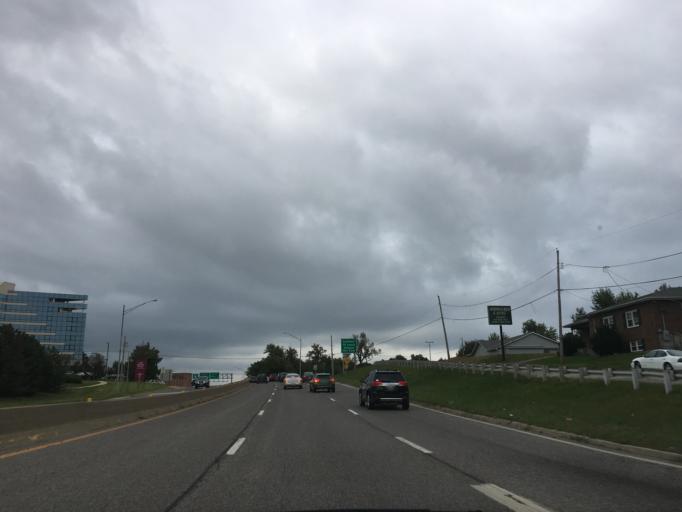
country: US
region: Missouri
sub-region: Saint Louis County
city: Saint Ann
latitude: 38.7390
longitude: -90.3978
